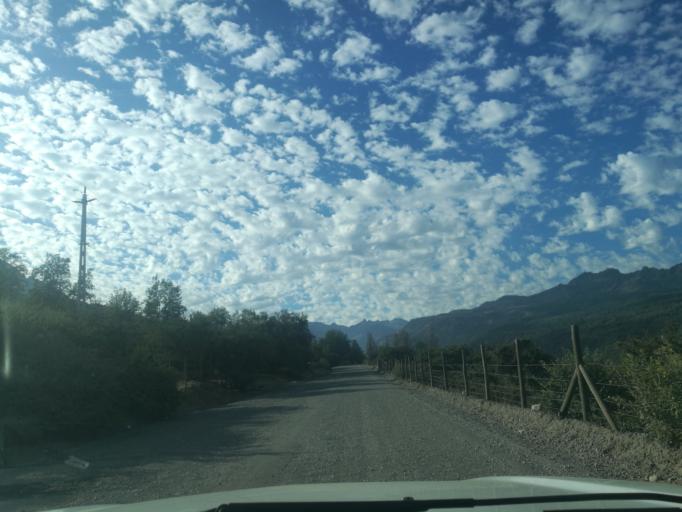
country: CL
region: O'Higgins
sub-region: Provincia de Cachapoal
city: Machali
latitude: -34.2590
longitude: -70.4616
